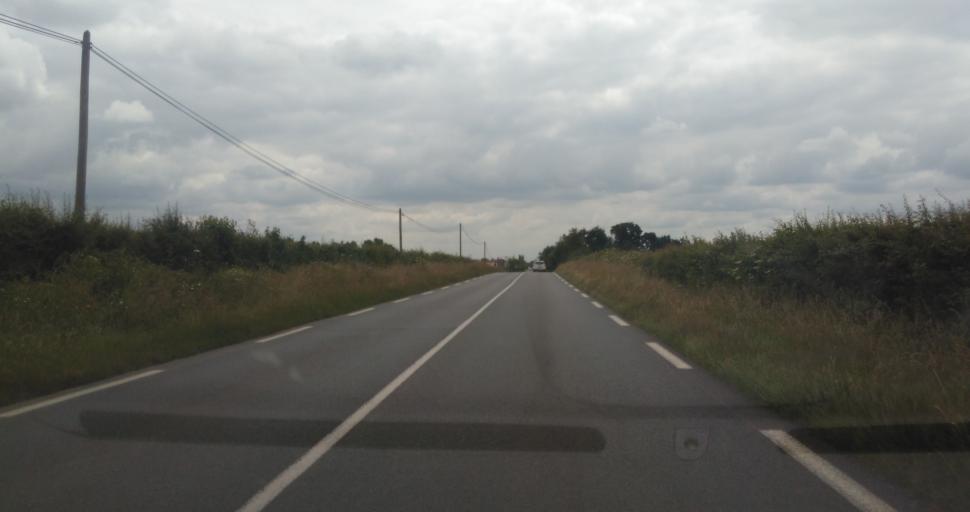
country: FR
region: Pays de la Loire
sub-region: Departement de la Vendee
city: Bournezeau
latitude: 46.6202
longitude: -1.1543
